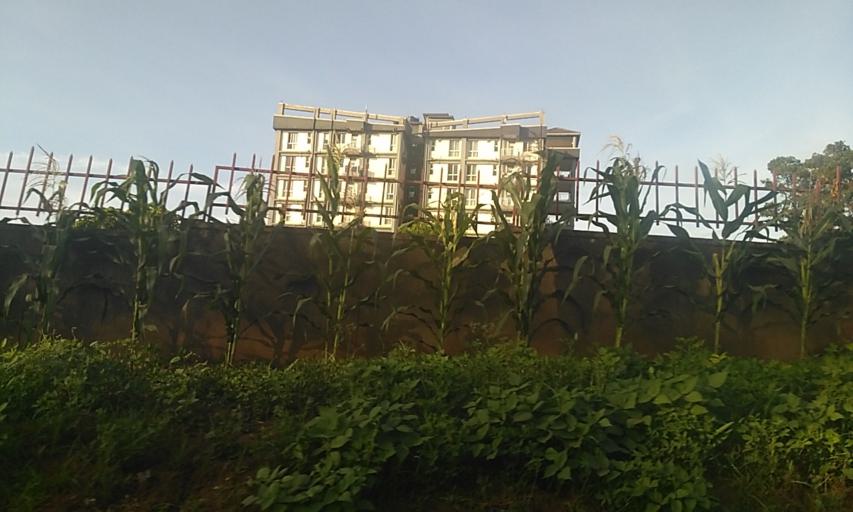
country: UG
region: Central Region
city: Kampala Central Division
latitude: 0.3527
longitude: 32.5937
